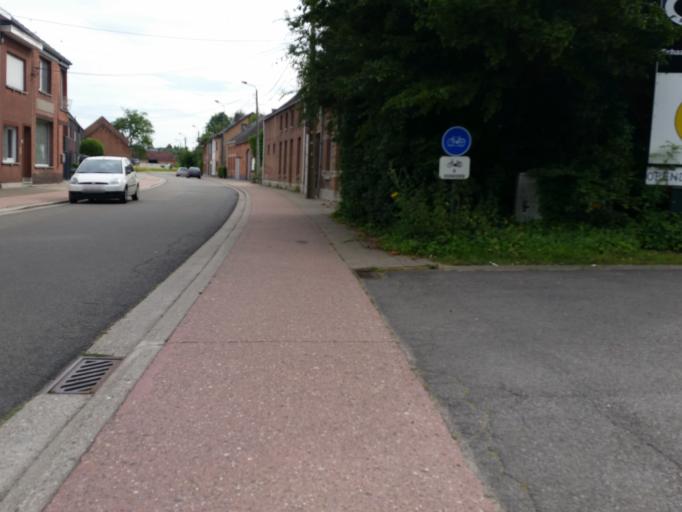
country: BE
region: Flanders
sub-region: Provincie Antwerpen
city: Willebroek
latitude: 51.0497
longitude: 4.3317
